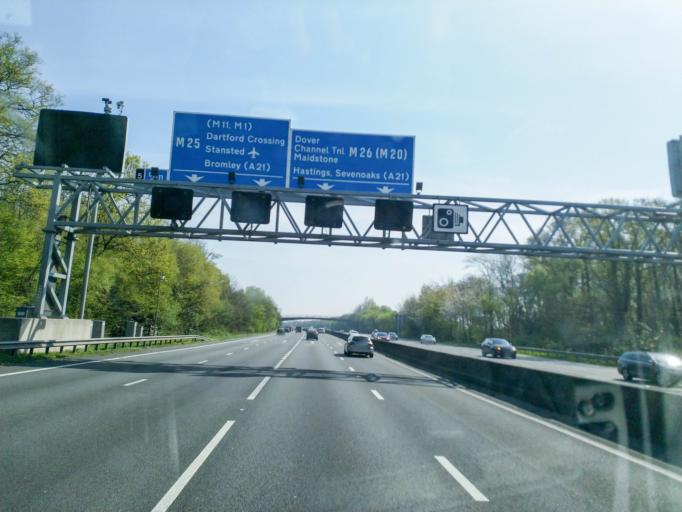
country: GB
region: England
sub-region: Kent
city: Halstead
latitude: 51.2855
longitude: 0.1127
